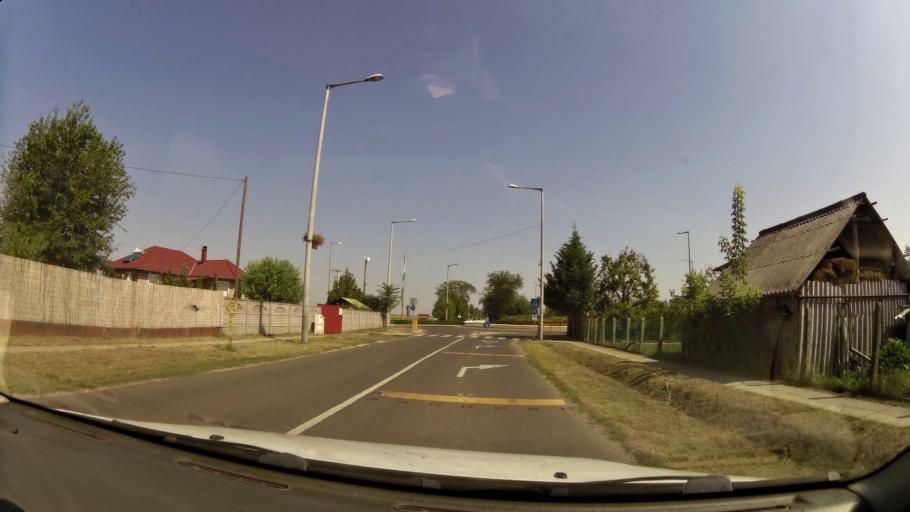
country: HU
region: Pest
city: Ujszilvas
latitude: 47.2778
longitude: 19.9237
